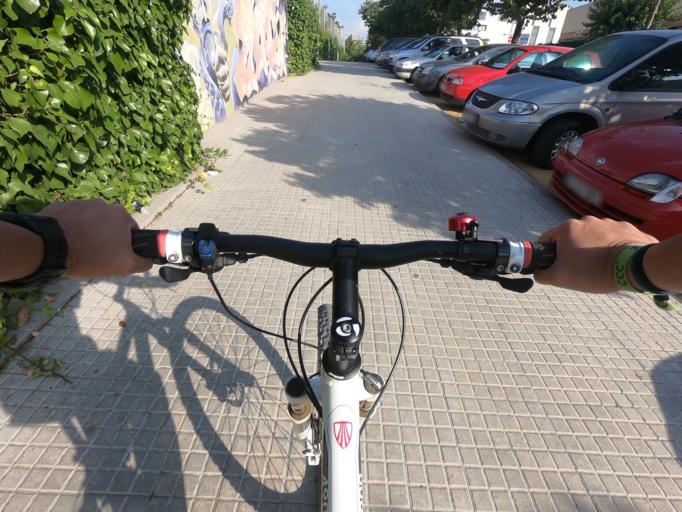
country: ES
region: Catalonia
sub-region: Provincia de Barcelona
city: Sant Just Desvern
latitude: 41.3824
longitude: 2.0684
